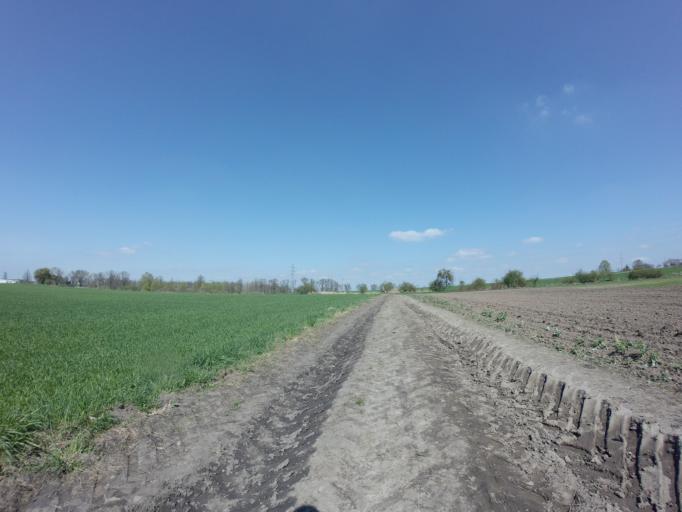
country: PL
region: West Pomeranian Voivodeship
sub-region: Powiat choszczenski
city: Choszczno
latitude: 53.1671
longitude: 15.4677
